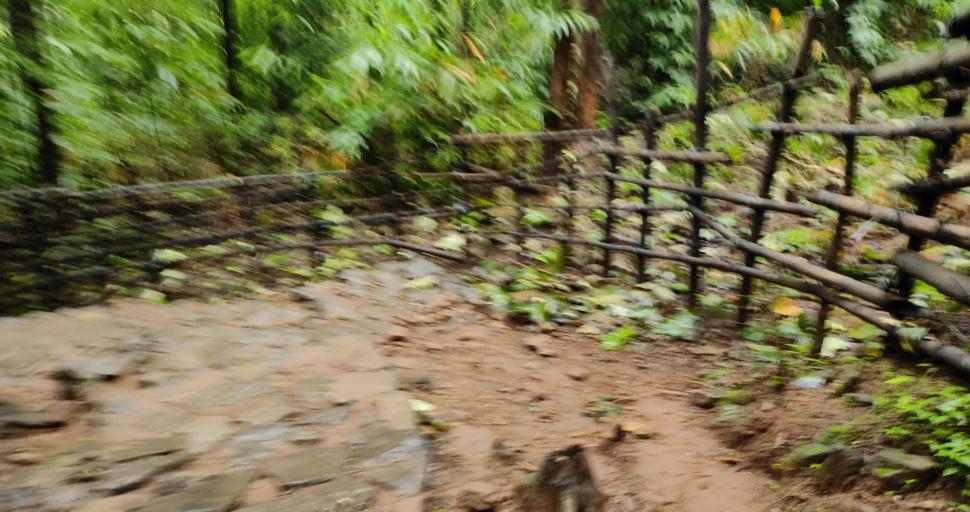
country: IN
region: Kerala
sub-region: Ernakulam
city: Angamali
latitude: 10.2865
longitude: 76.5699
